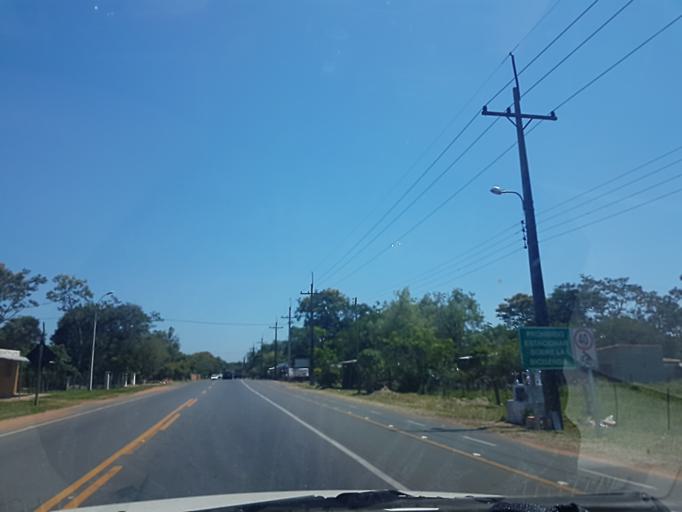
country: PY
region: Central
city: Aregua
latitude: -25.2368
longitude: -57.4218
